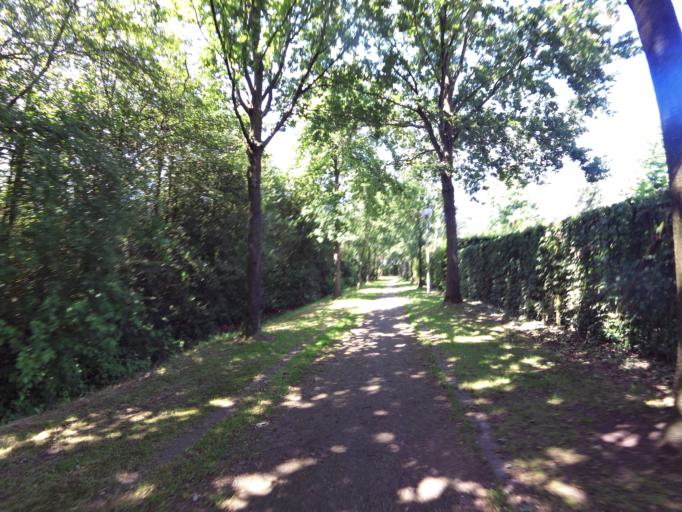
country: BE
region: Flanders
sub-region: Provincie West-Vlaanderen
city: Zedelgem
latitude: 51.1888
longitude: 3.1673
